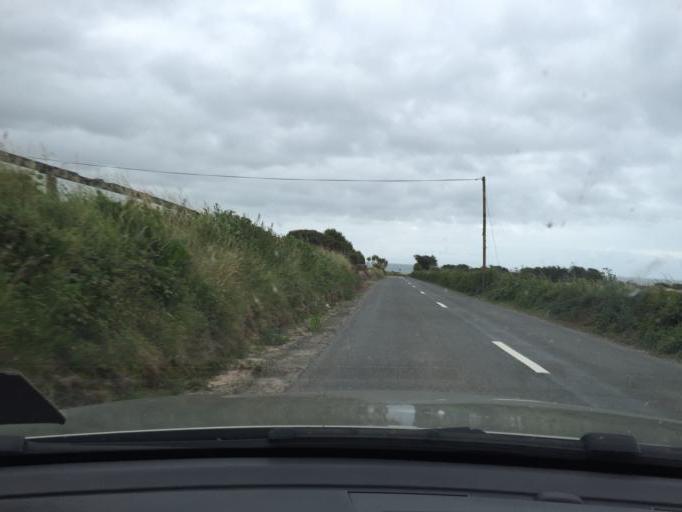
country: IE
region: Munster
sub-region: County Cork
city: Youghal
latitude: 51.9638
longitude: -7.7193
